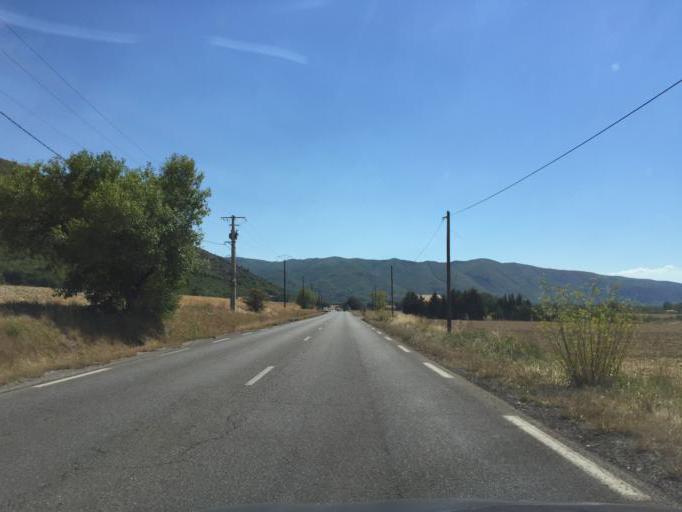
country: FR
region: Provence-Alpes-Cote d'Azur
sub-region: Departement des Alpes-de-Haute-Provence
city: Malijai
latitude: 44.0667
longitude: 6.0218
